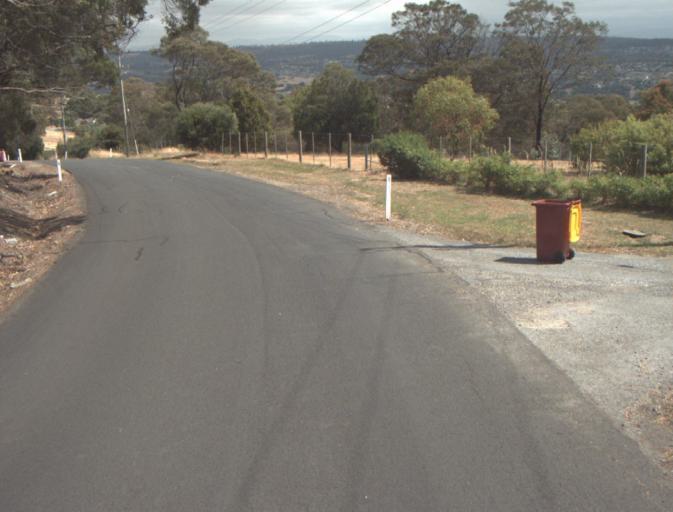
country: AU
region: Tasmania
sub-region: Launceston
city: Newstead
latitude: -41.4455
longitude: 147.2117
